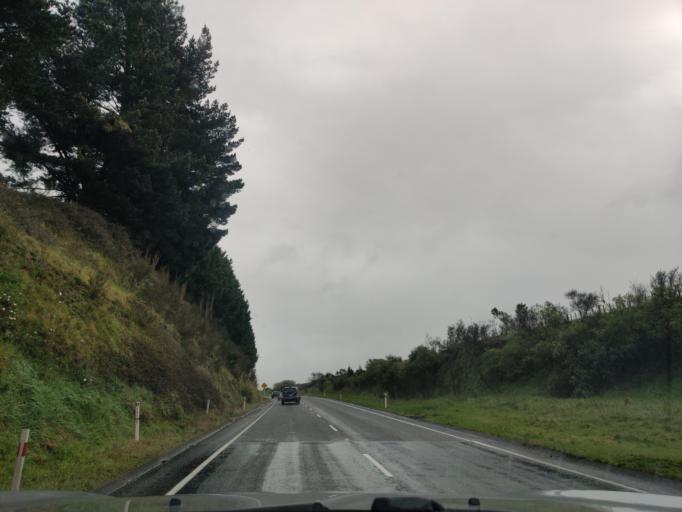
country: NZ
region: Manawatu-Wanganui
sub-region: Palmerston North City
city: Palmerston North
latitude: -40.0545
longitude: 176.2360
